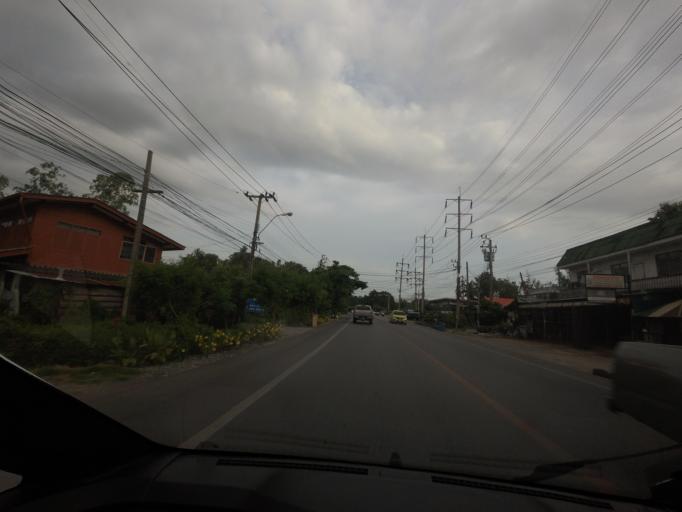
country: TH
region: Bangkok
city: Nong Chok
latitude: 13.8622
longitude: 100.8607
